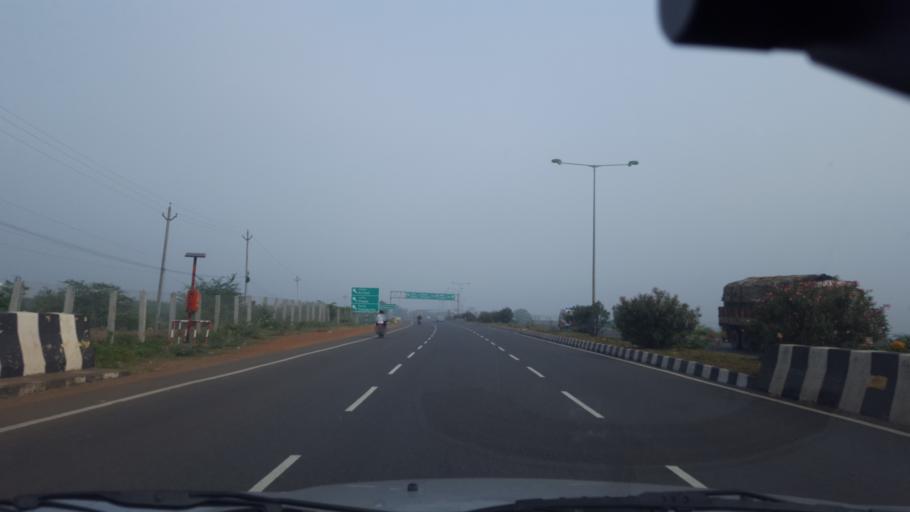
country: IN
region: Andhra Pradesh
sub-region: Prakasam
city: Ongole
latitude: 15.4639
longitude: 80.0483
